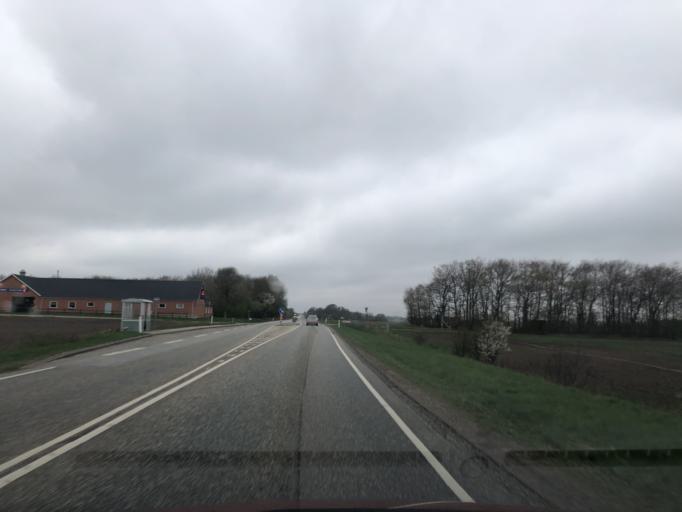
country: DK
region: Central Jutland
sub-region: Holstebro Kommune
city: Holstebro
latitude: 56.3215
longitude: 8.6749
